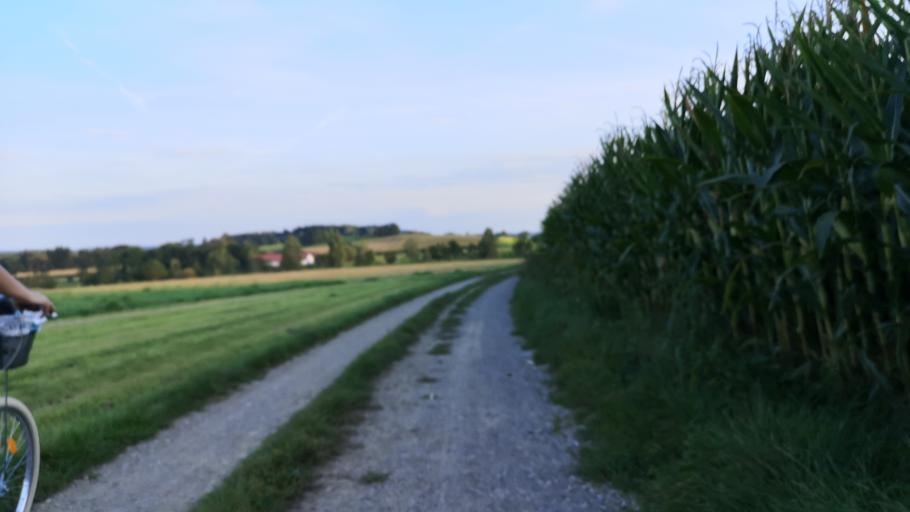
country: DE
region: Bavaria
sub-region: Upper Bavaria
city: Poing
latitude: 48.1593
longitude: 11.8234
